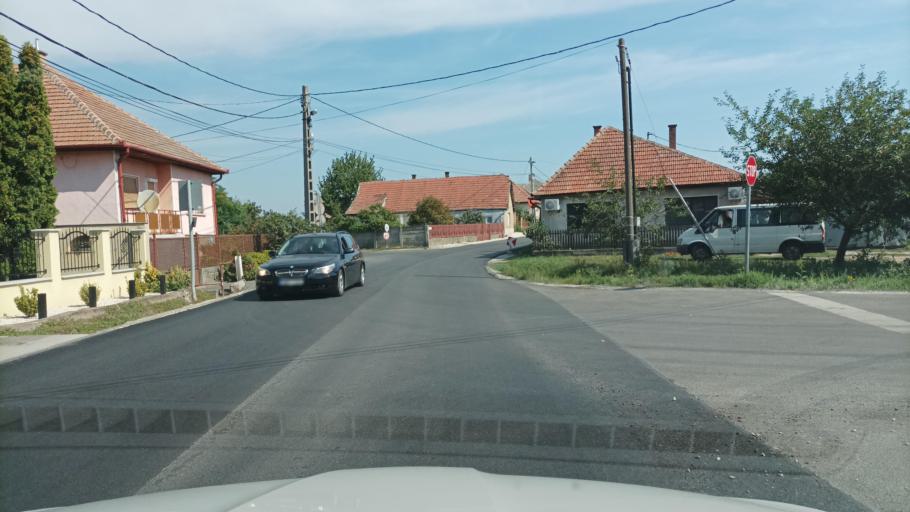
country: HU
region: Pest
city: Tura
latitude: 47.6065
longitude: 19.5966
